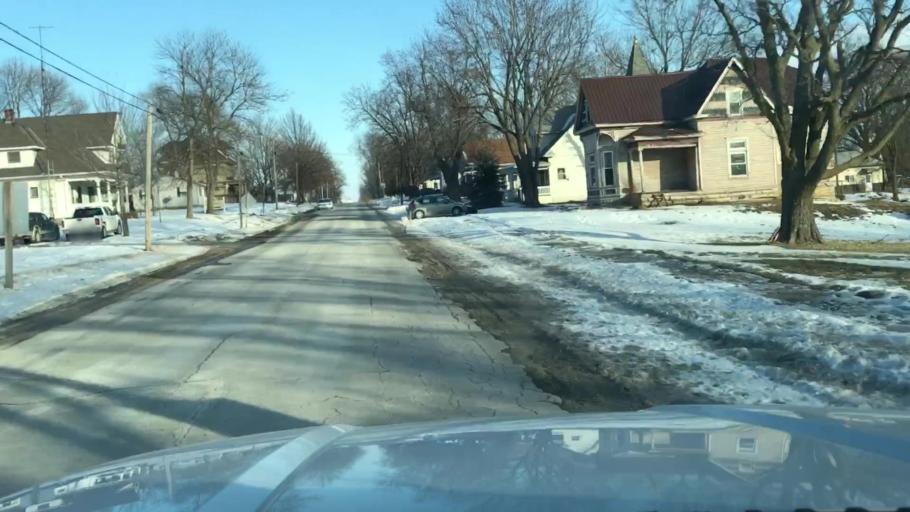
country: US
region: Missouri
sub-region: Andrew County
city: Savannah
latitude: 40.0251
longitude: -94.9725
